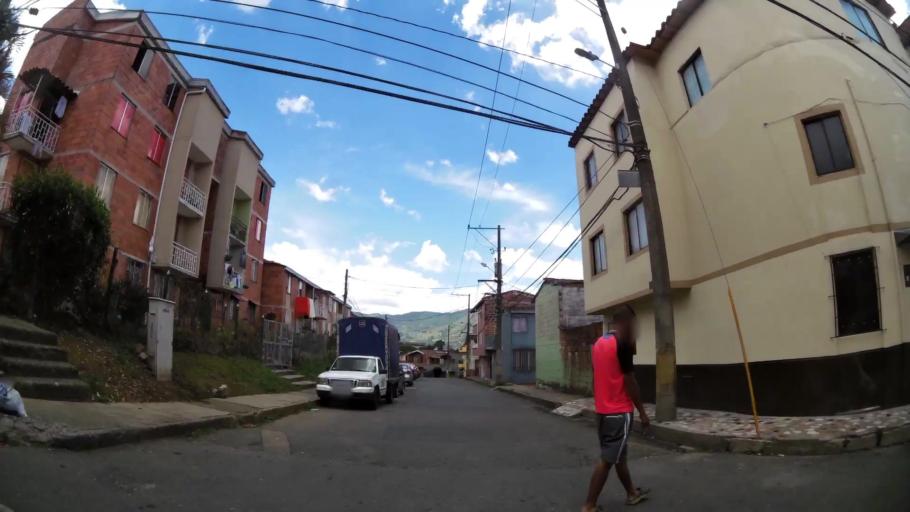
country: CO
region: Antioquia
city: La Estrella
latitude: 6.1533
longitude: -75.6396
